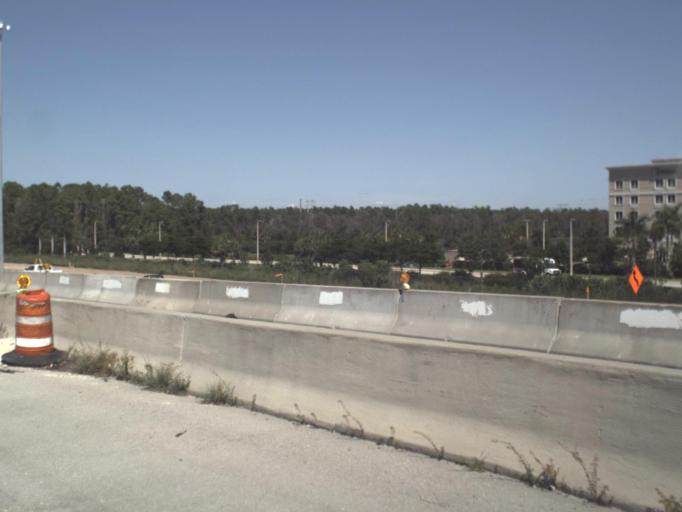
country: US
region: Florida
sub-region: Lee County
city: Three Oaks
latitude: 26.4957
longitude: -81.7943
